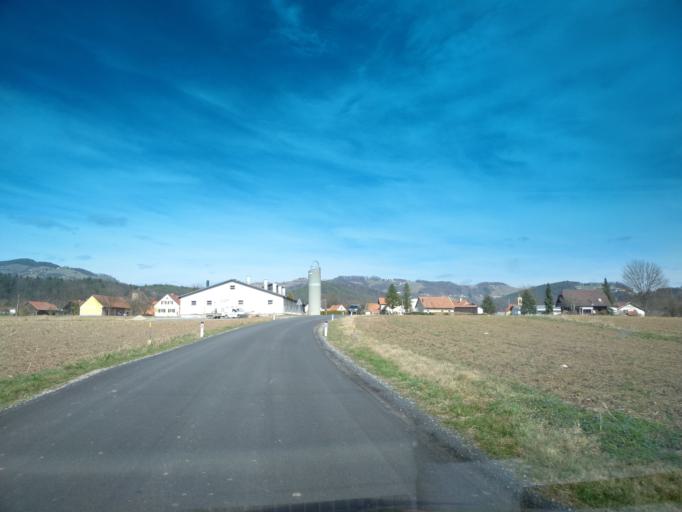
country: AT
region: Styria
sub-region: Politischer Bezirk Leibnitz
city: Grossklein
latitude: 46.7496
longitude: 15.4373
